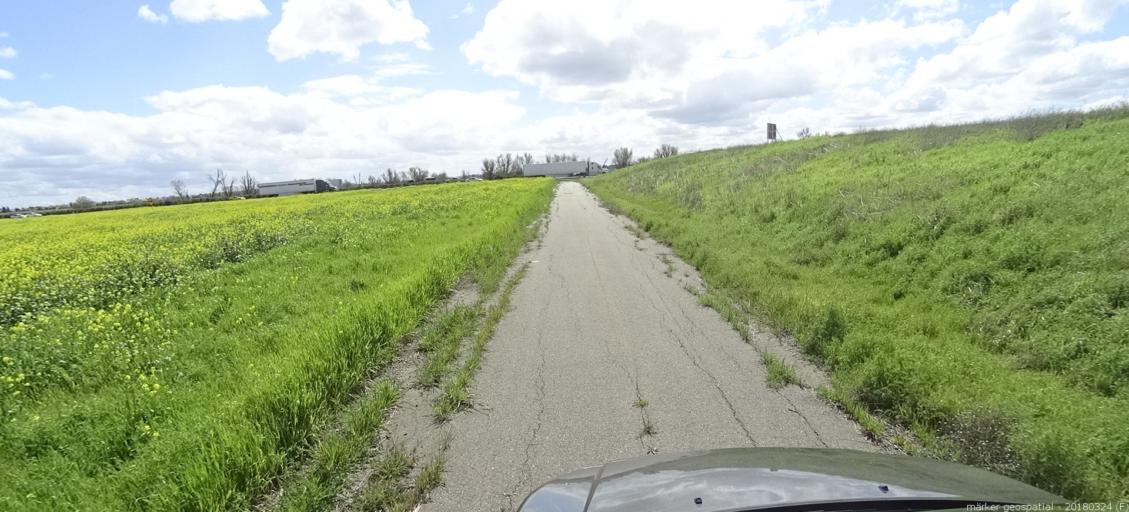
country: US
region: California
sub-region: Yolo County
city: West Sacramento
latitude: 38.6727
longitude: -121.5603
